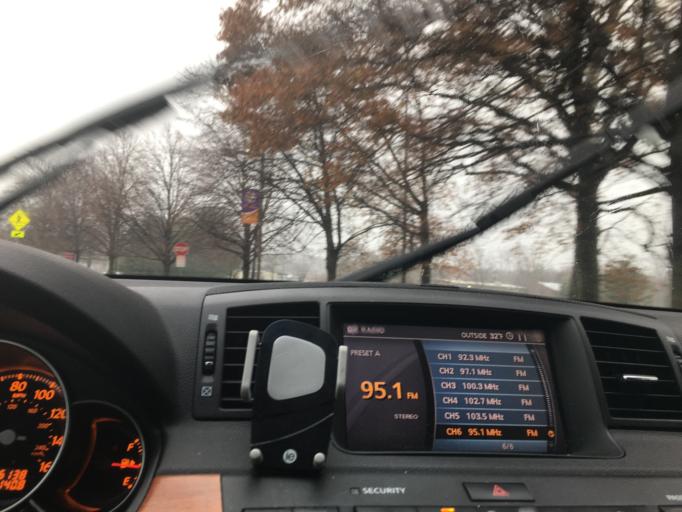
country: US
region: New Jersey
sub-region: Bergen County
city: Paramus
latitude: 40.9529
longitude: -74.0919
